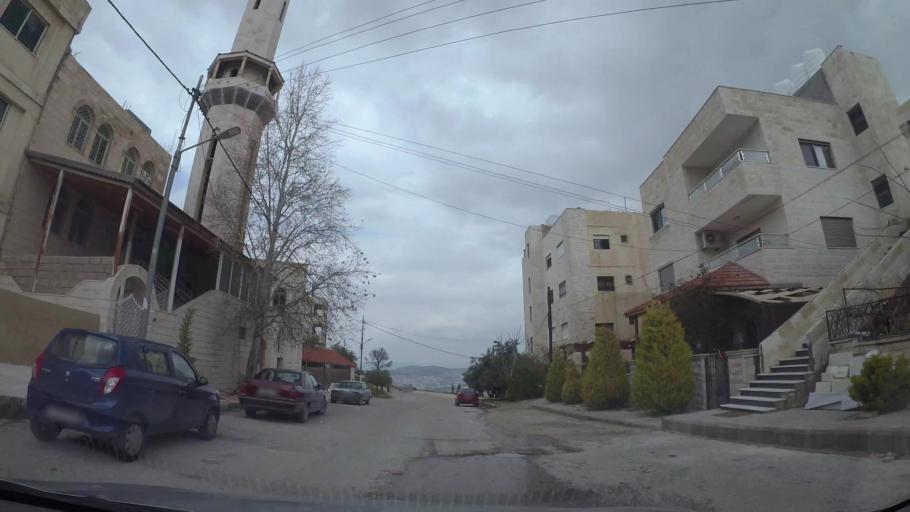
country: JO
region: Amman
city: Al Jubayhah
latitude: 32.0381
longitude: 35.8281
